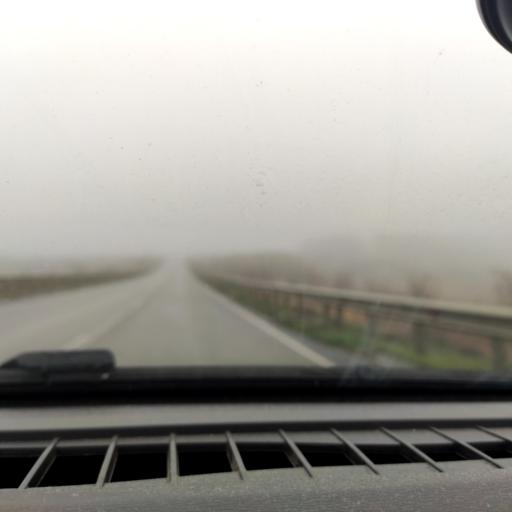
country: RU
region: Belgorod
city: Ilovka
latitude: 50.7671
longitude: 38.7519
